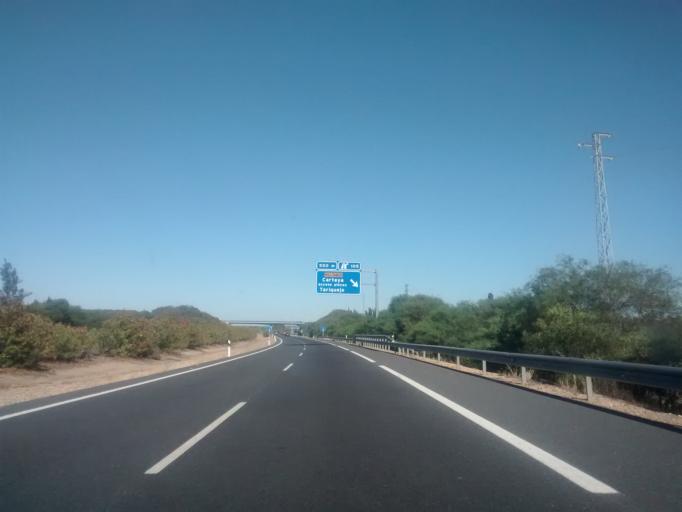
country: ES
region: Andalusia
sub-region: Provincia de Huelva
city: Cartaya
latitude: 37.3295
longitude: -7.1411
